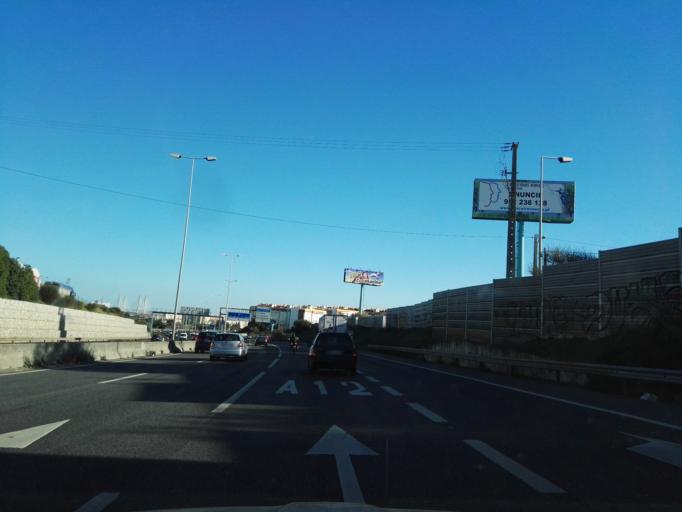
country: PT
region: Lisbon
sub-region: Loures
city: Camarate
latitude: 38.7971
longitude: -9.1229
